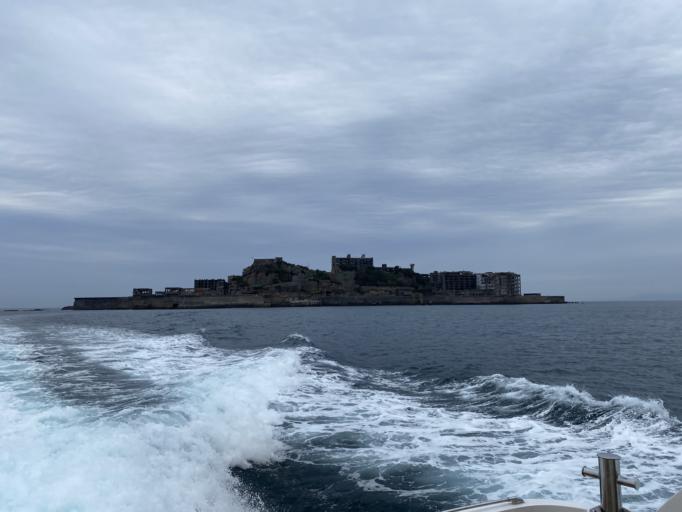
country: JP
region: Nagasaki
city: Nagasaki-shi
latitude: 32.6241
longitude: 129.7418
